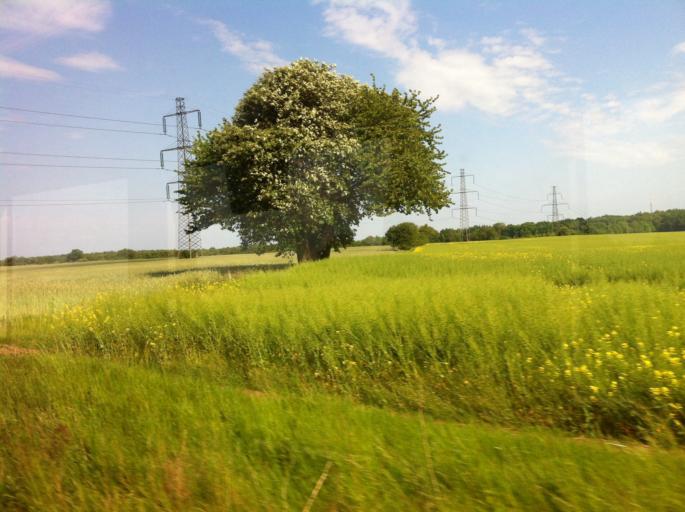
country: DK
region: Capital Region
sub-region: Helsingor Kommune
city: Hornbaek
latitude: 56.0758
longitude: 12.5018
